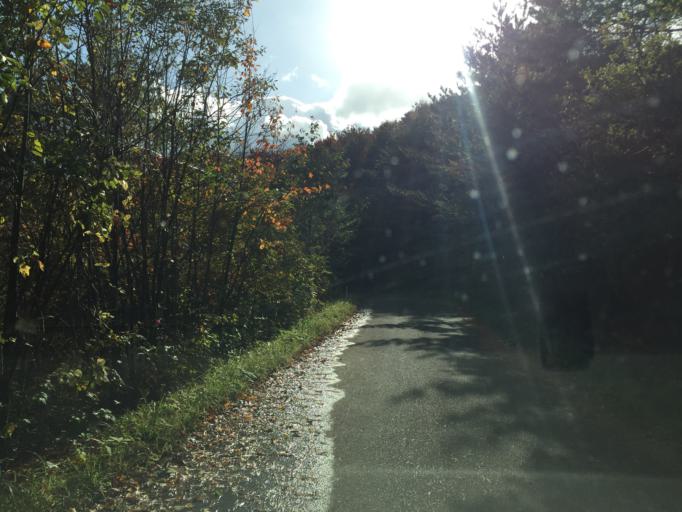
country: JP
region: Fukushima
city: Fukushima-shi
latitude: 37.7098
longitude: 140.3173
